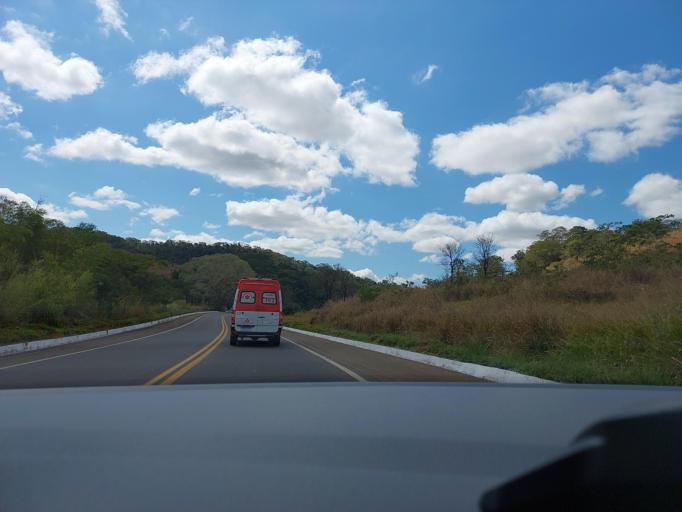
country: BR
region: Minas Gerais
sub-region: Muriae
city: Muriae
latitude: -21.1355
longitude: -42.2979
